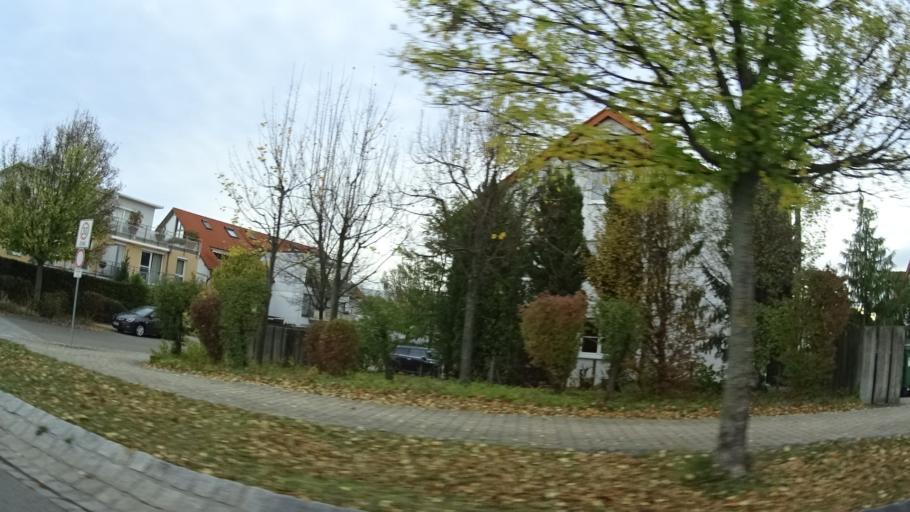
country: DE
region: Baden-Wuerttemberg
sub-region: Regierungsbezirk Stuttgart
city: Gerlingen
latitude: 48.7989
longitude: 9.0535
